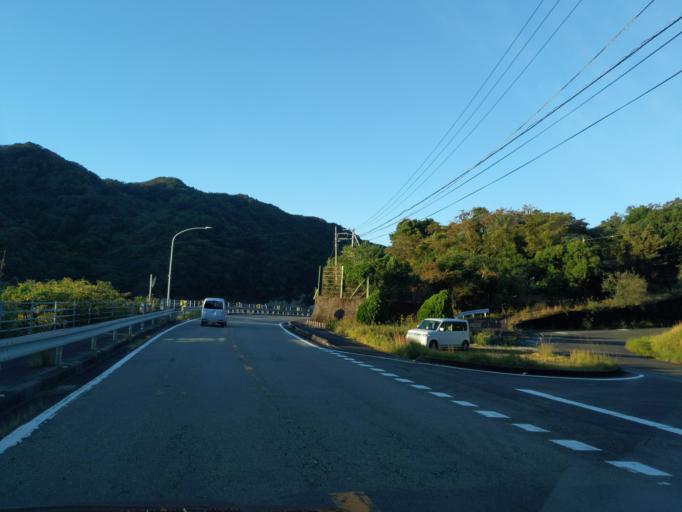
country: JP
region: Kochi
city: Muroto-misakicho
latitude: 33.5866
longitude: 134.3506
